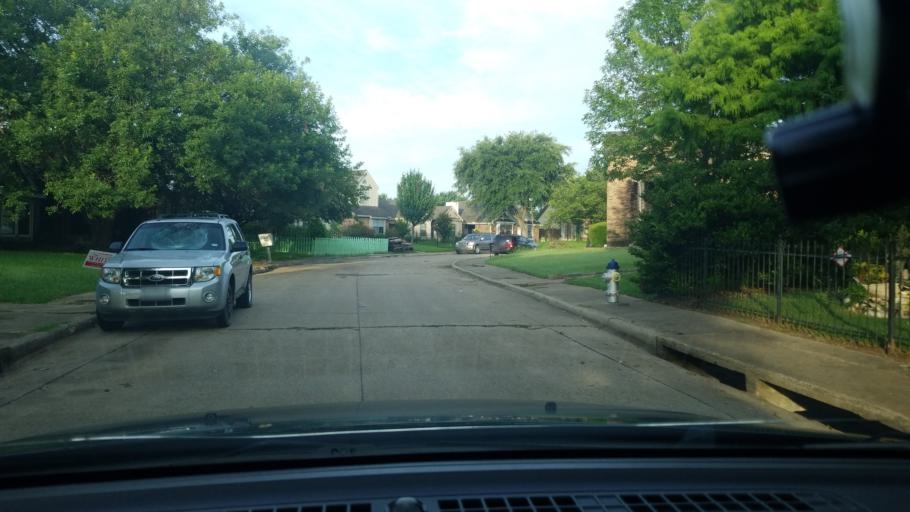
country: US
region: Texas
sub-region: Dallas County
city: Balch Springs
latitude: 32.7547
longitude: -96.6420
